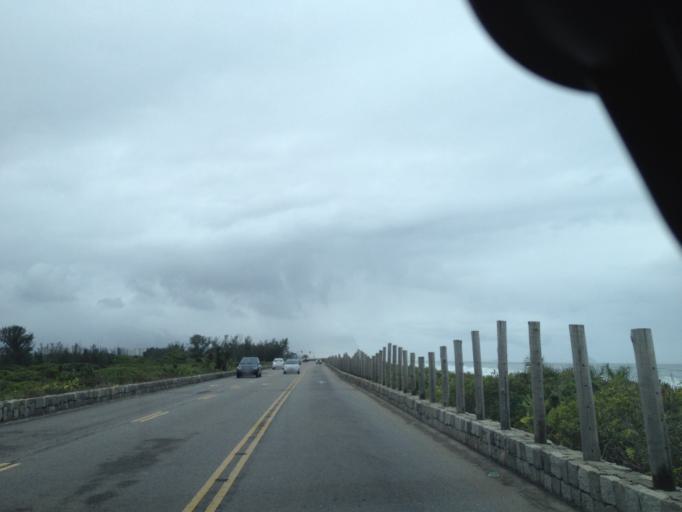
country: BR
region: Rio de Janeiro
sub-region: Nilopolis
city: Nilopolis
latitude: -23.0192
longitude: -43.4320
